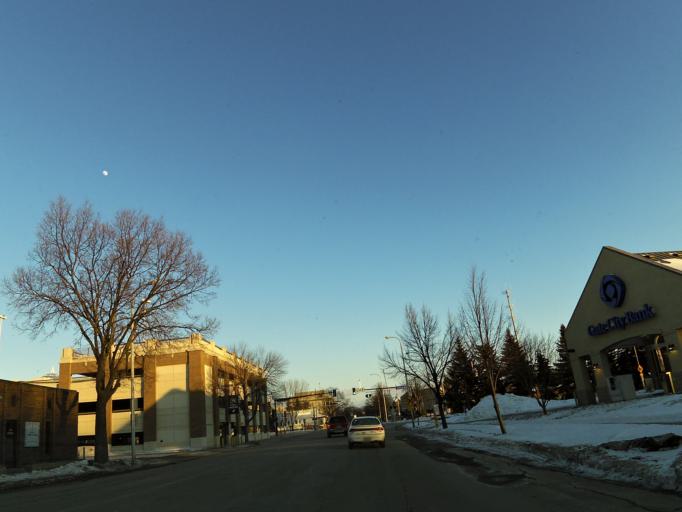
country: US
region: North Dakota
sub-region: Grand Forks County
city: Grand Forks
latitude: 47.9236
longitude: -97.0324
